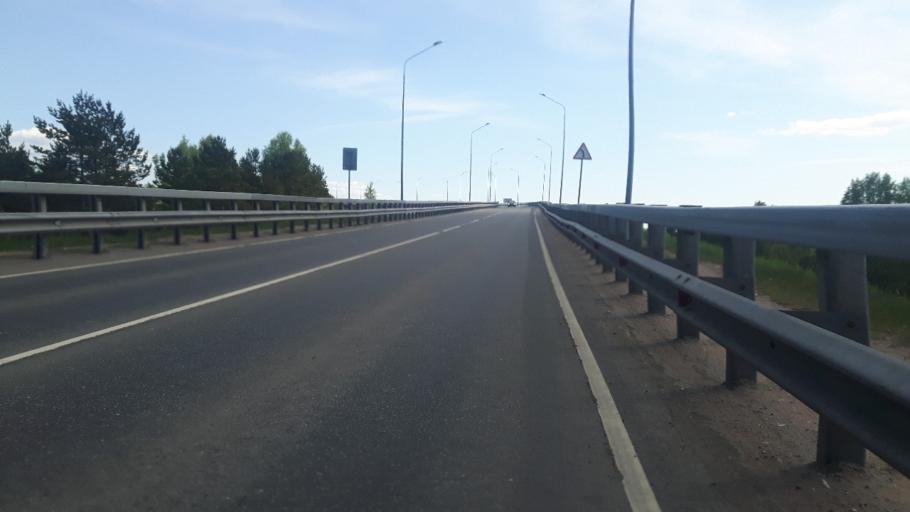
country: RU
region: Leningrad
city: Vyborg
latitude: 60.7414
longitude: 28.6824
